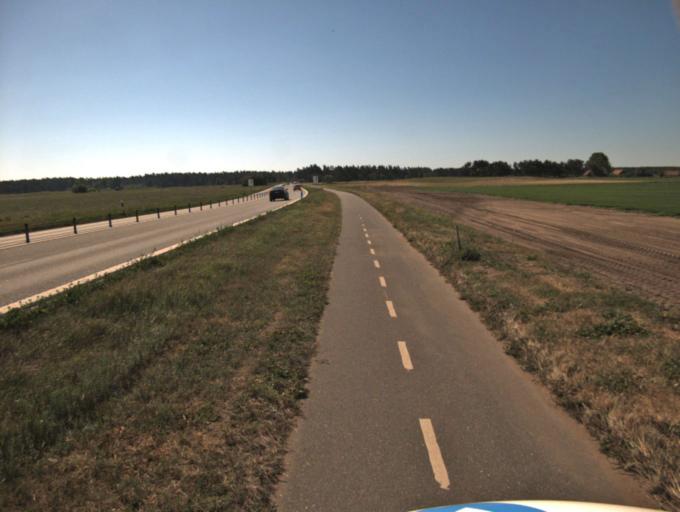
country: SE
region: Skane
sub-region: Kristianstads Kommun
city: Ahus
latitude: 55.9694
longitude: 14.2751
